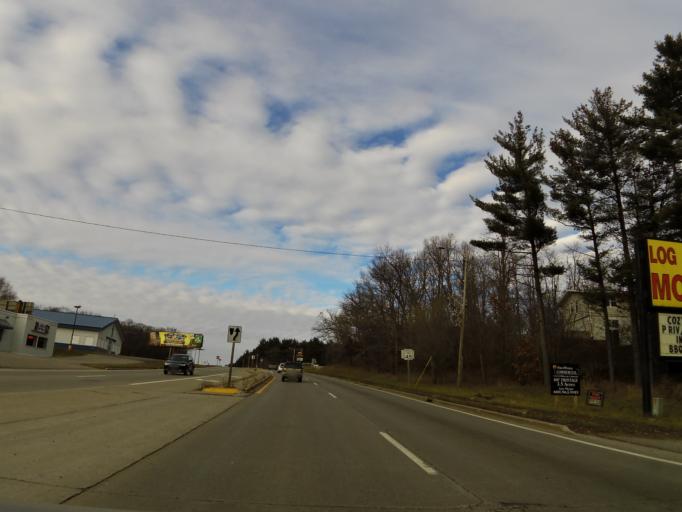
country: US
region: Wisconsin
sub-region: Sauk County
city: West Baraboo
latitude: 43.4788
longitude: -89.7691
